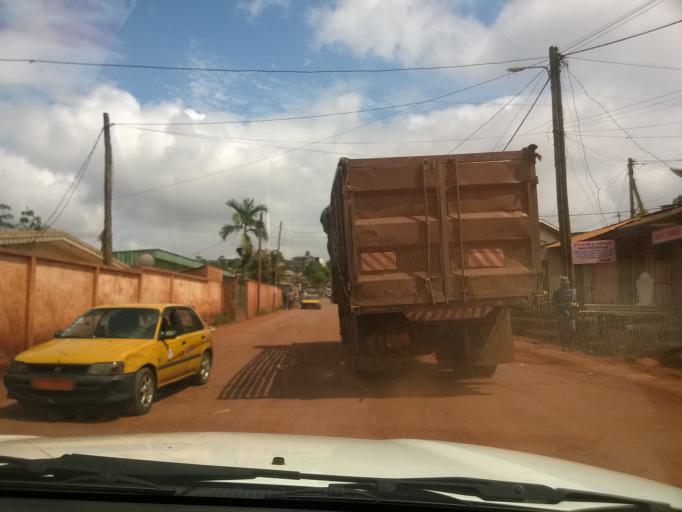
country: CM
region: Centre
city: Yaounde
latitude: 3.8711
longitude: 11.5423
